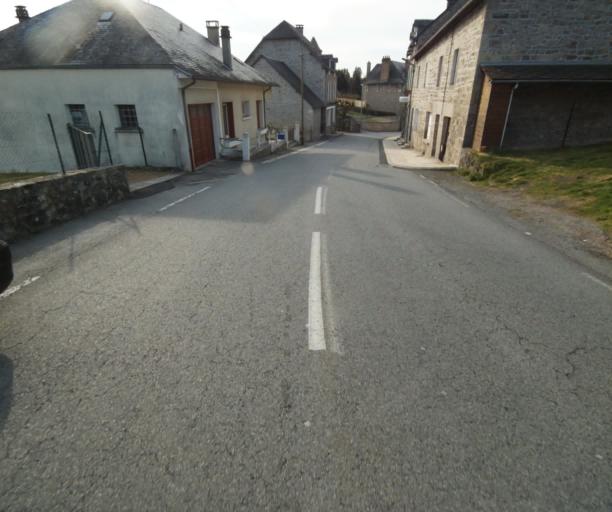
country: FR
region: Limousin
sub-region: Departement de la Correze
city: Correze
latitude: 45.3742
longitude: 1.8736
